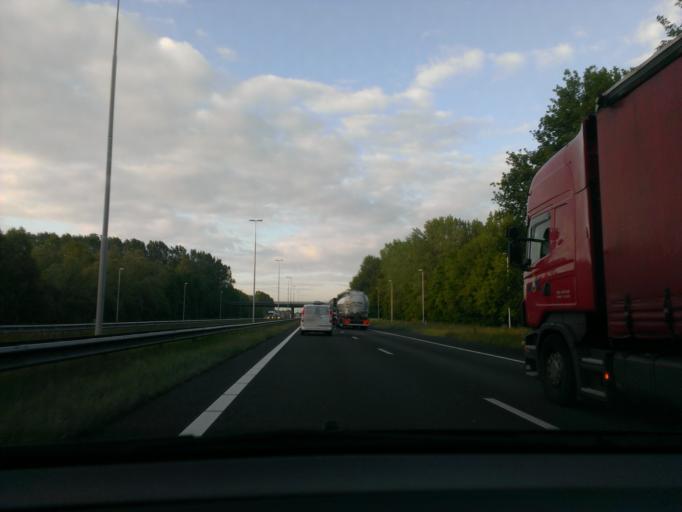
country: NL
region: Gelderland
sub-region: Gemeente Epe
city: Emst
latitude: 52.2934
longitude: 6.0093
